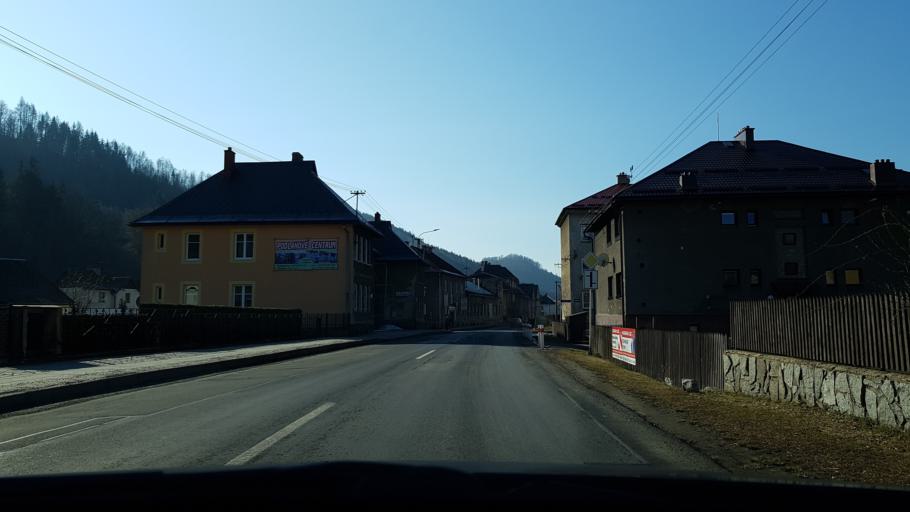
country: CZ
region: Olomoucky
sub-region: Okres Sumperk
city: Hanusovice
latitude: 50.0724
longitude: 16.9320
